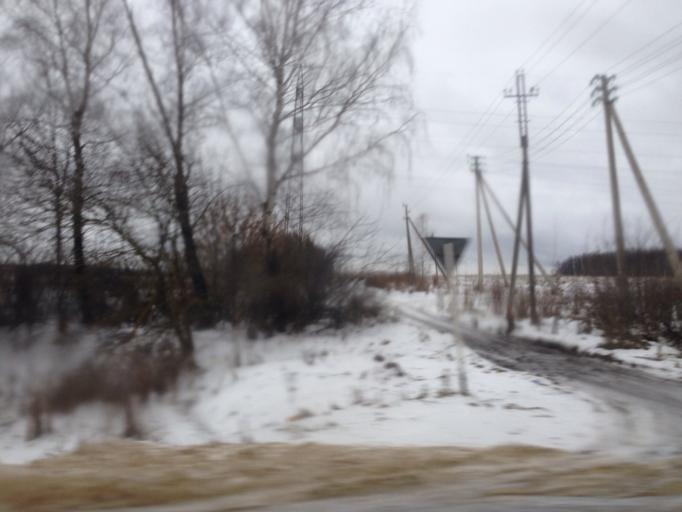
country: RU
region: Tula
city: Skuratovskiy
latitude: 54.1195
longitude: 37.7060
